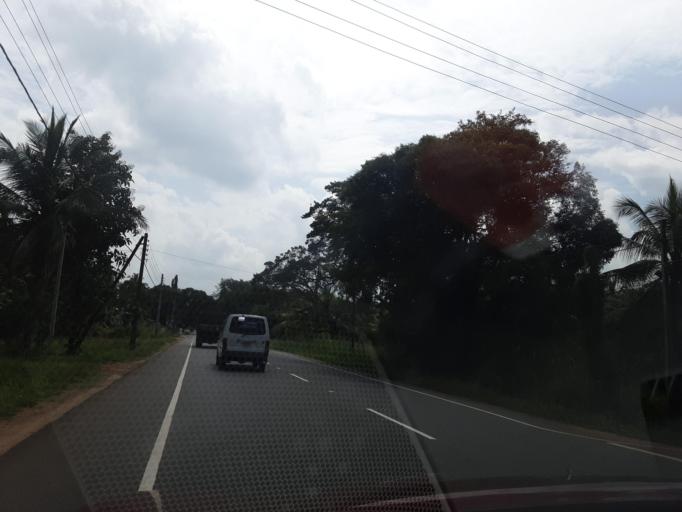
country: LK
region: North Central
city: Anuradhapura
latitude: 8.4869
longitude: 80.5106
